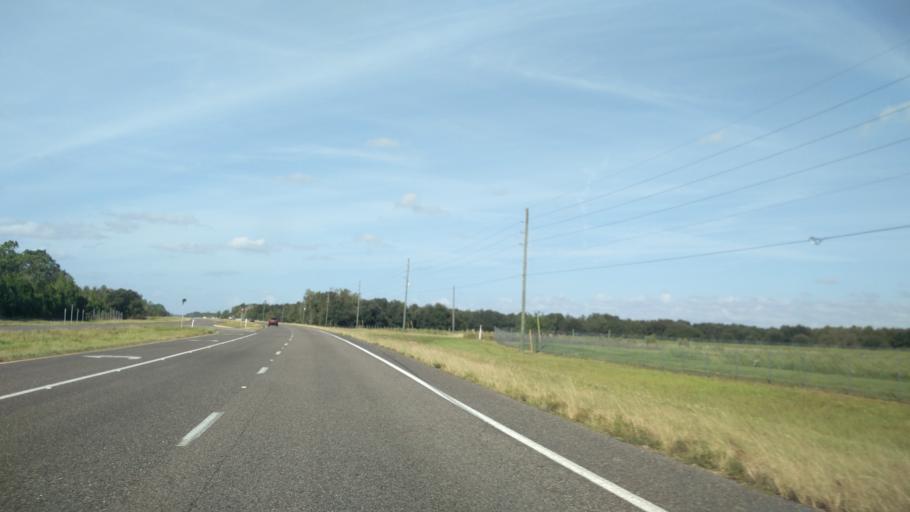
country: US
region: Florida
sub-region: Brevard County
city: June Park
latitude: 28.1160
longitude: -80.9276
